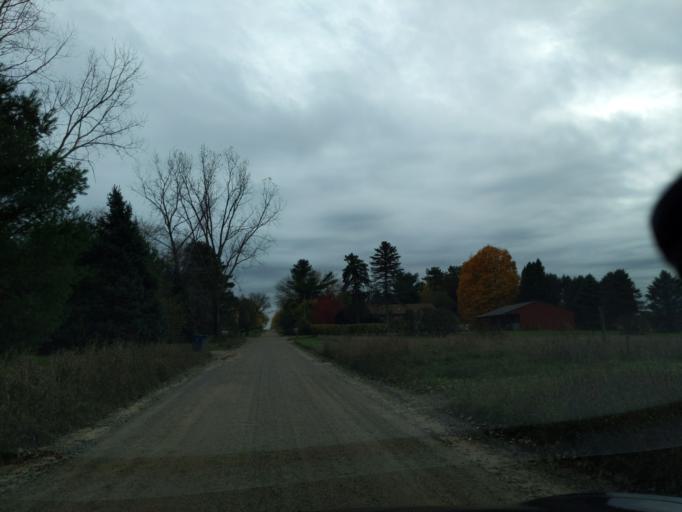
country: US
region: Michigan
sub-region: Eaton County
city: Eaton Rapids
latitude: 42.5421
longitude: -84.6213
